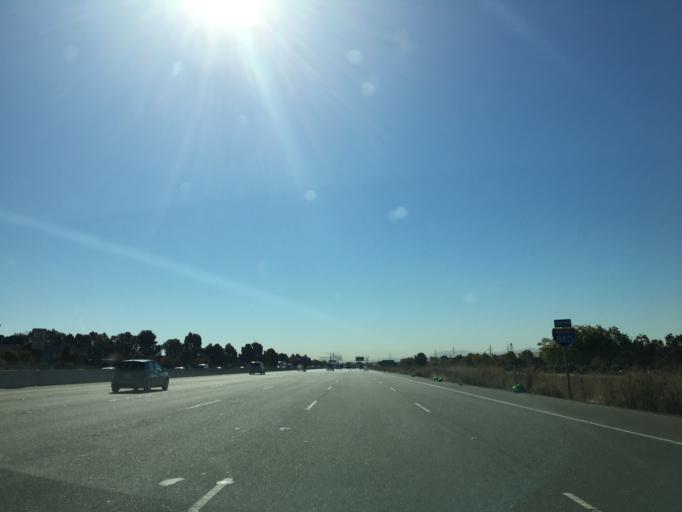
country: US
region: California
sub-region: Santa Clara County
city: Milpitas
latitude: 37.4751
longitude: -121.9323
